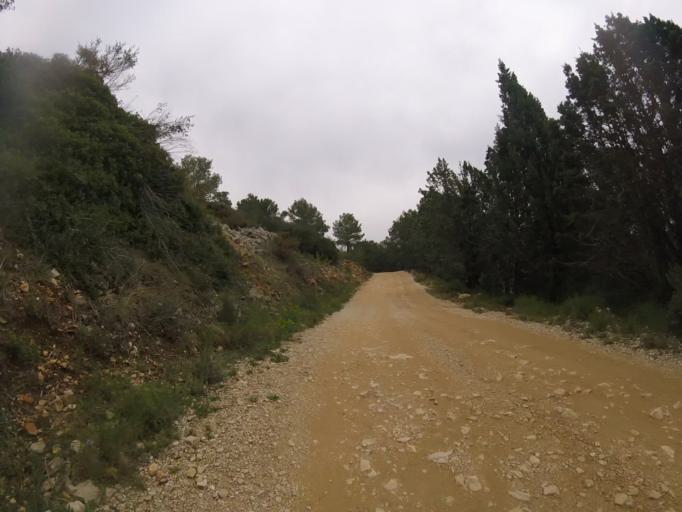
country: ES
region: Valencia
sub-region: Provincia de Castello
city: Alcala de Xivert
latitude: 40.3038
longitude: 0.2559
